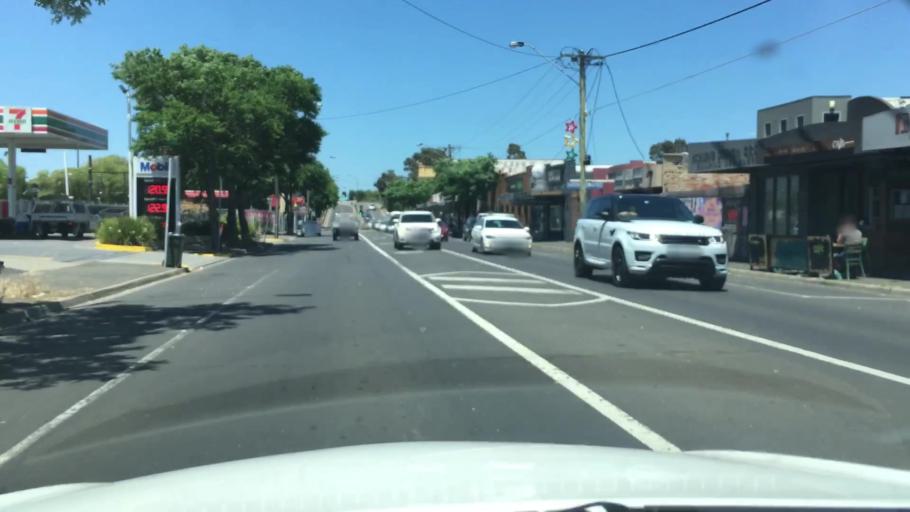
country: AU
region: Victoria
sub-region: Hobsons Bay
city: Newport
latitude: -37.8407
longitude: 144.8829
